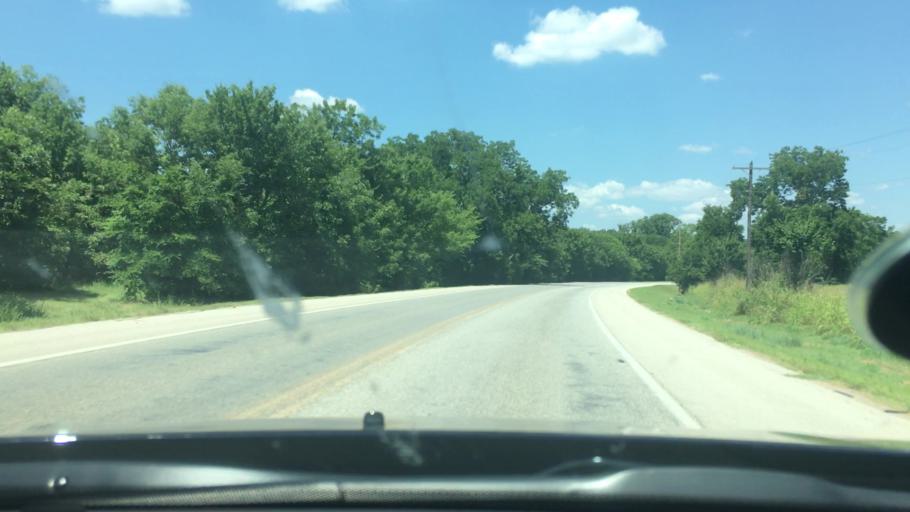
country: US
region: Oklahoma
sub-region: Marshall County
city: Oakland
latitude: 34.1736
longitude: -96.8531
